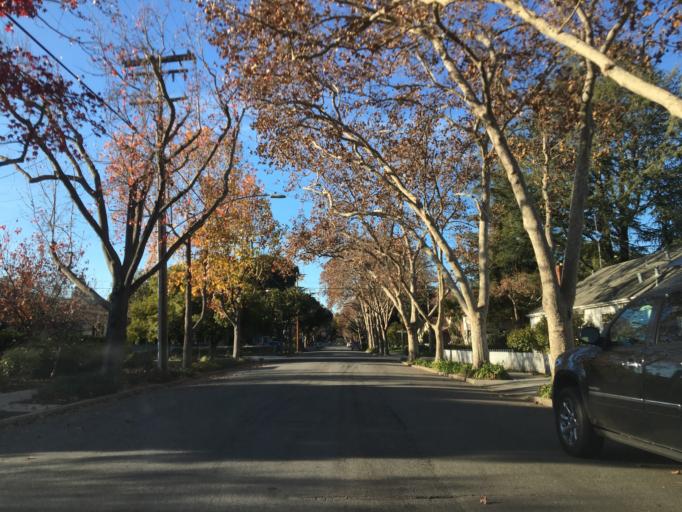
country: US
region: California
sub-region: Santa Clara County
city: Palo Alto
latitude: 37.4378
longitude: -122.1424
